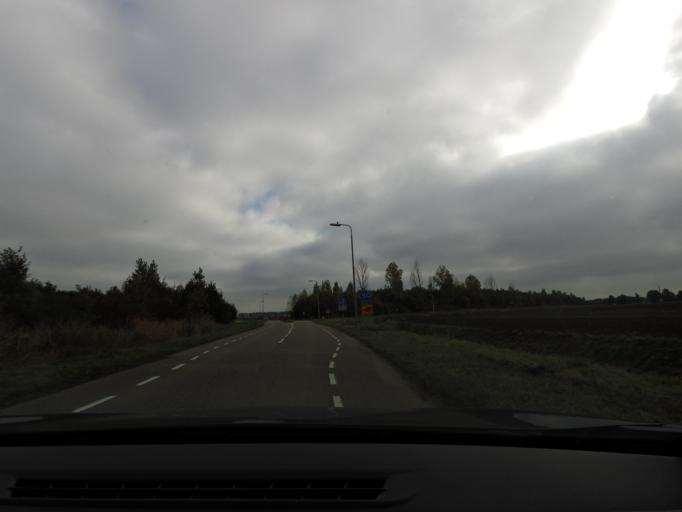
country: NL
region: South Holland
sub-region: Gemeente Oud-Beijerland
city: Oud-Beijerland
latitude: 51.7599
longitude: 4.3718
